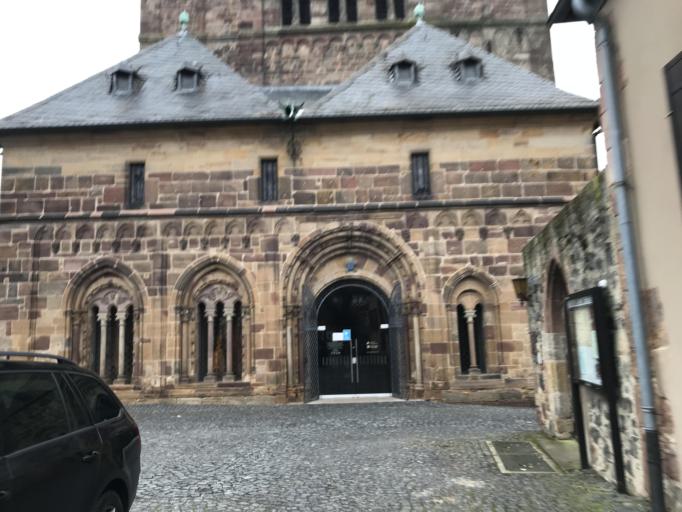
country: DE
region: Hesse
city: Fritzlar
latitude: 51.1307
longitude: 9.2730
